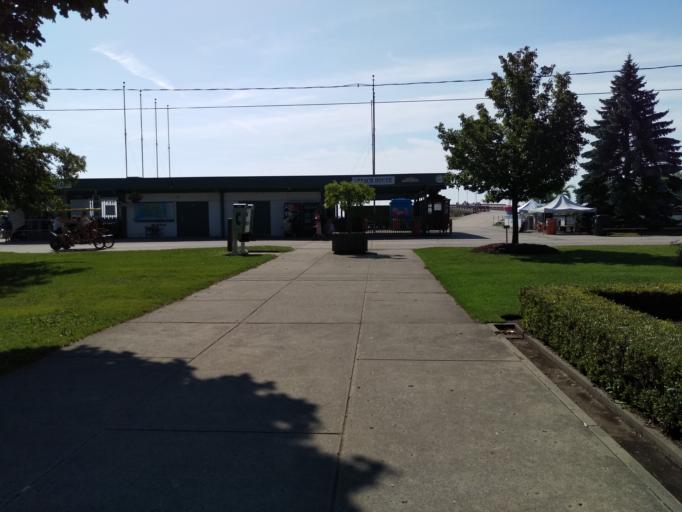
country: CA
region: Ontario
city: Toronto
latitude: 43.6173
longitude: -79.3723
